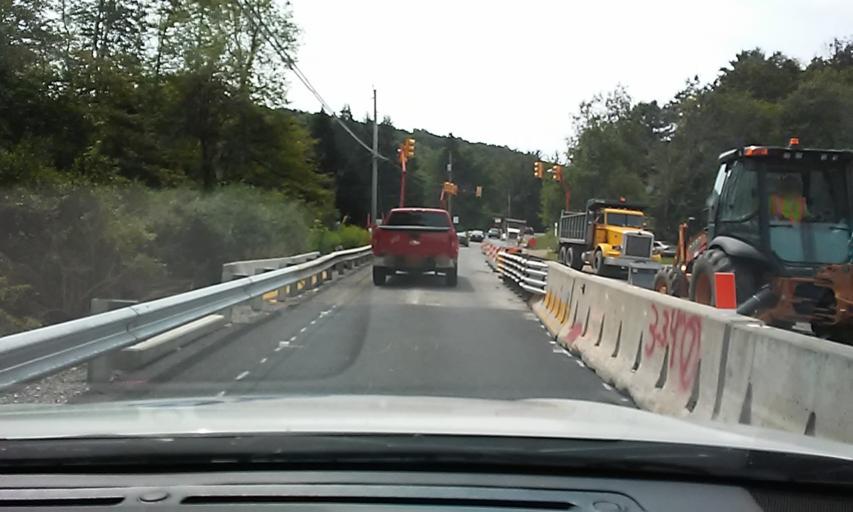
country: US
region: Pennsylvania
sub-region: Clearfield County
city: Treasure Lake
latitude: 41.1856
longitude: -78.6054
